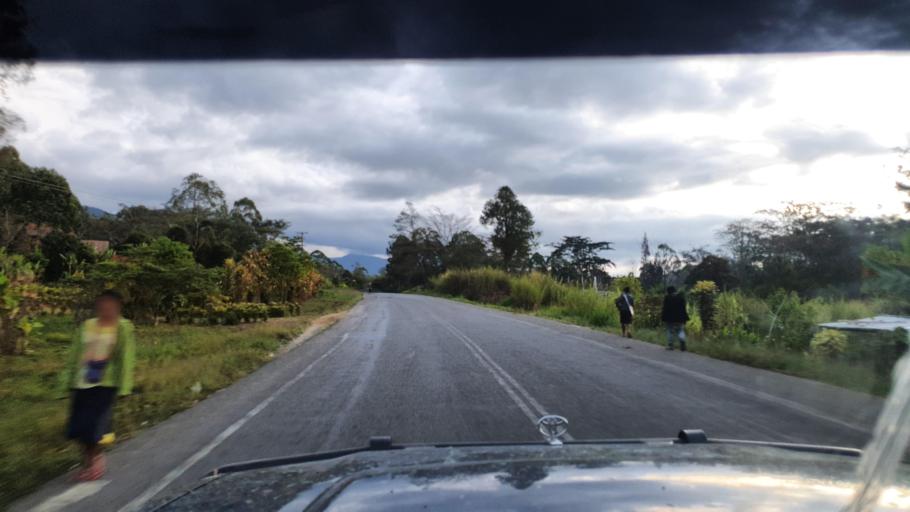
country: PG
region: Jiwaka
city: Minj
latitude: -5.8351
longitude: 144.5449
